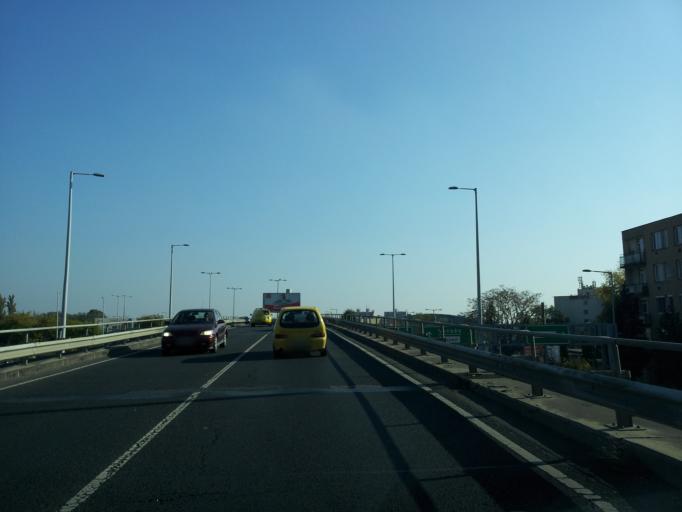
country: HU
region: Budapest
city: Budapest XIX. keruelet
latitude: 47.4662
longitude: 19.1240
